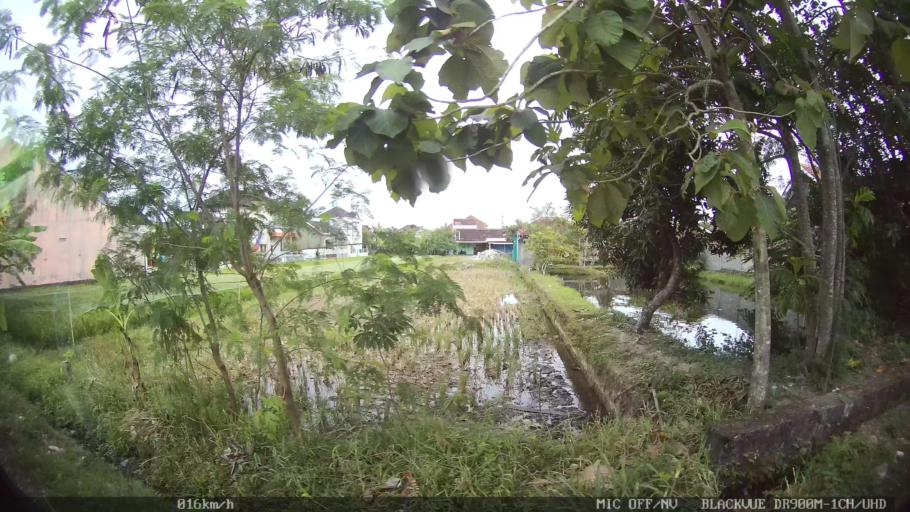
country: ID
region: Daerah Istimewa Yogyakarta
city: Depok
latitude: -7.8182
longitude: 110.4205
